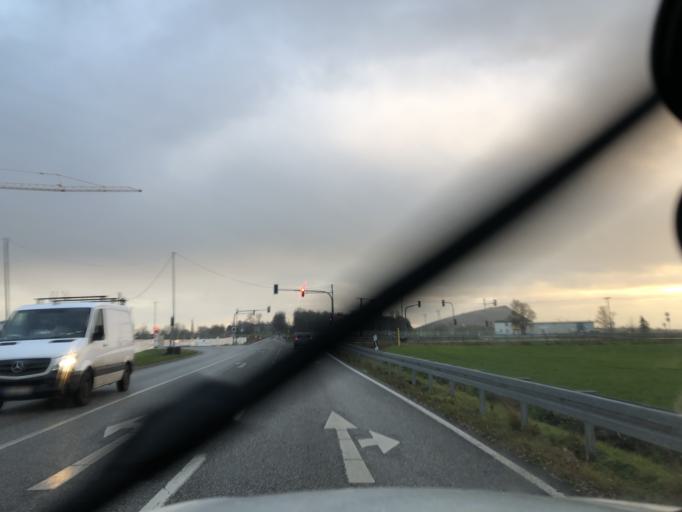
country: DE
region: Saxony-Anhalt
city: Langenbogen
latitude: 51.4790
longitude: 11.7800
